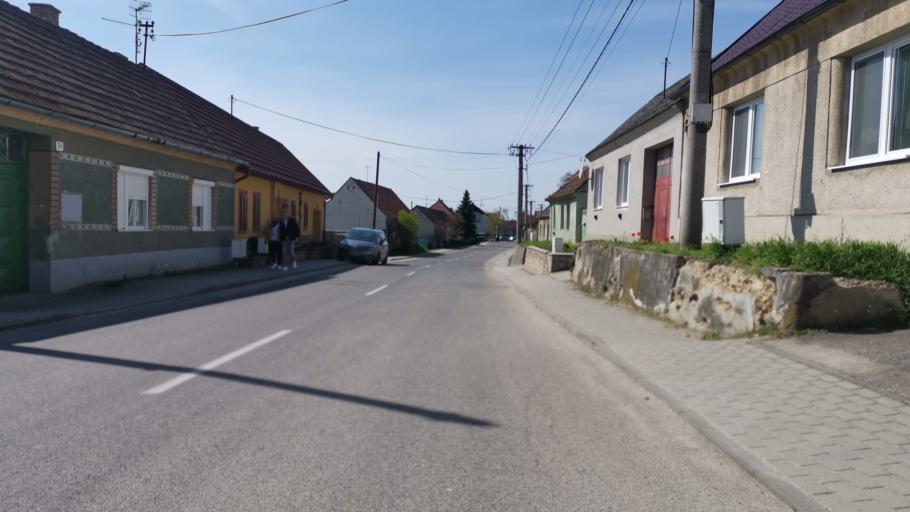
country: SK
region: Trnavsky
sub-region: Okres Skalica
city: Holic
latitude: 48.7507
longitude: 17.1980
